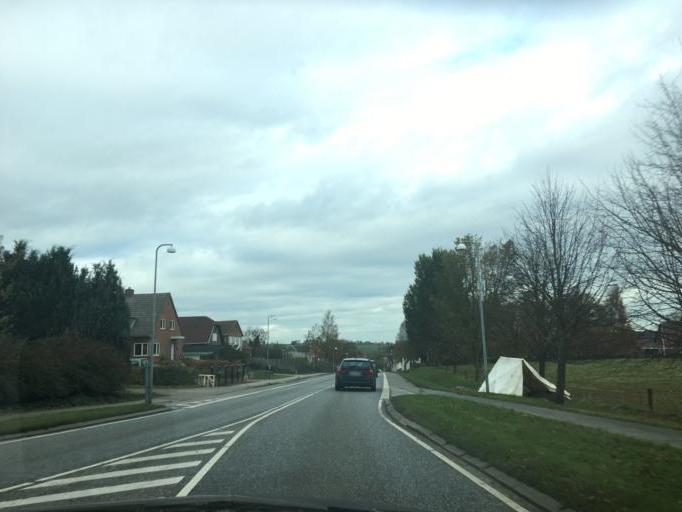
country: DK
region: South Denmark
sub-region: Vejle Kommune
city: Vejle
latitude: 55.6542
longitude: 9.5046
